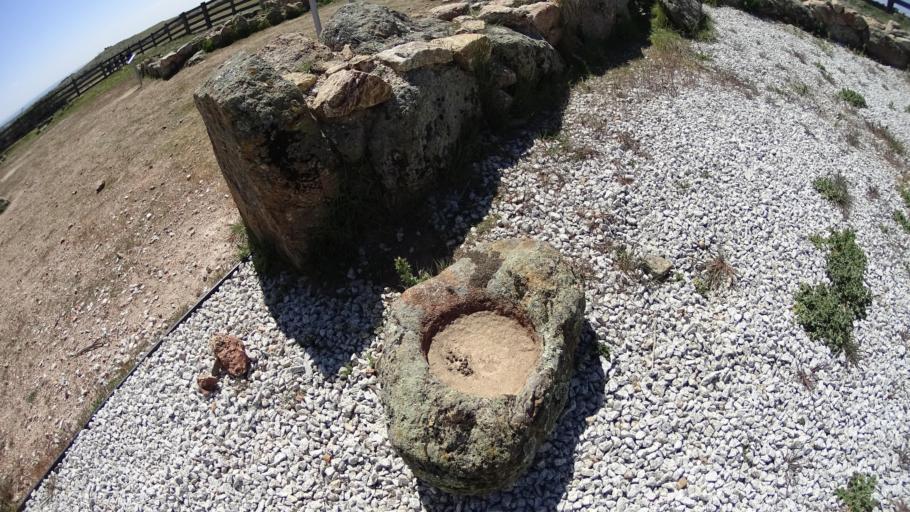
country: ES
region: Madrid
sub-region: Provincia de Madrid
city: Colmenar Viejo
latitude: 40.7008
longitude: -3.7508
